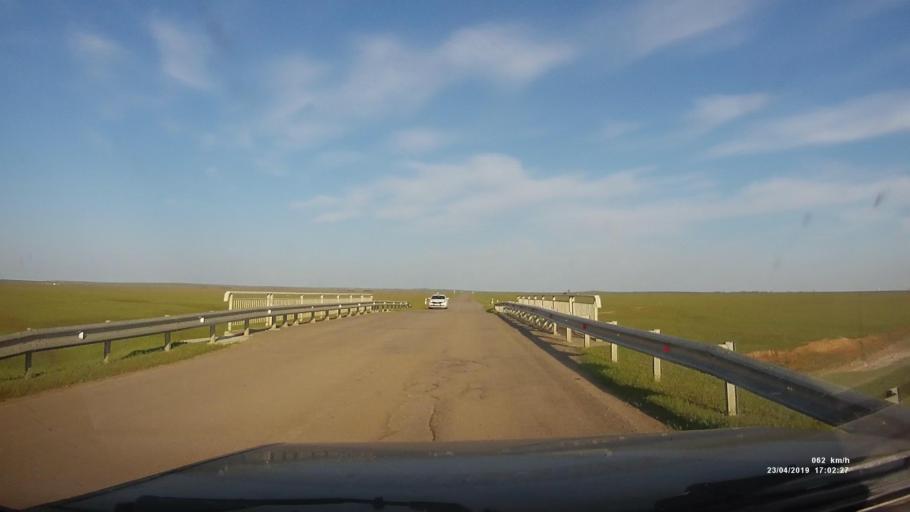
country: RU
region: Kalmykiya
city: Priyutnoye
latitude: 46.2926
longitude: 43.4178
